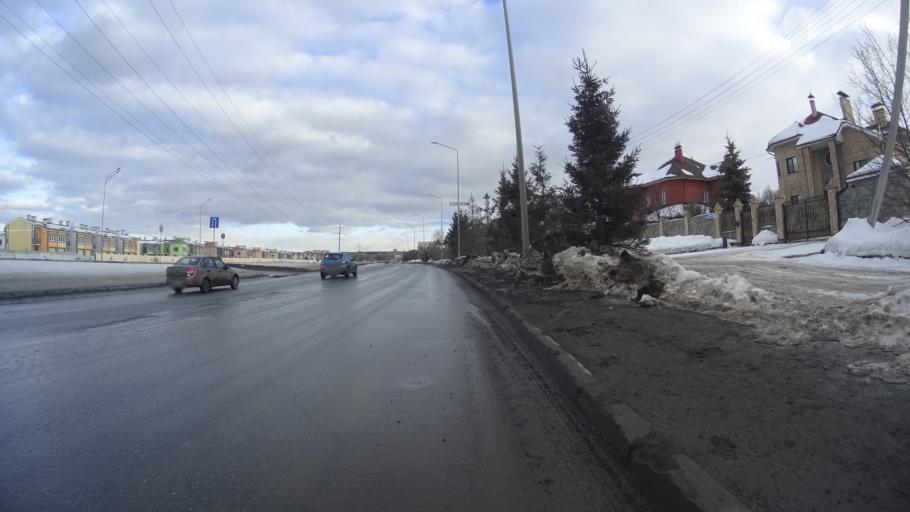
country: RU
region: Chelyabinsk
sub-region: Gorod Chelyabinsk
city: Chelyabinsk
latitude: 55.1563
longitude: 61.3083
